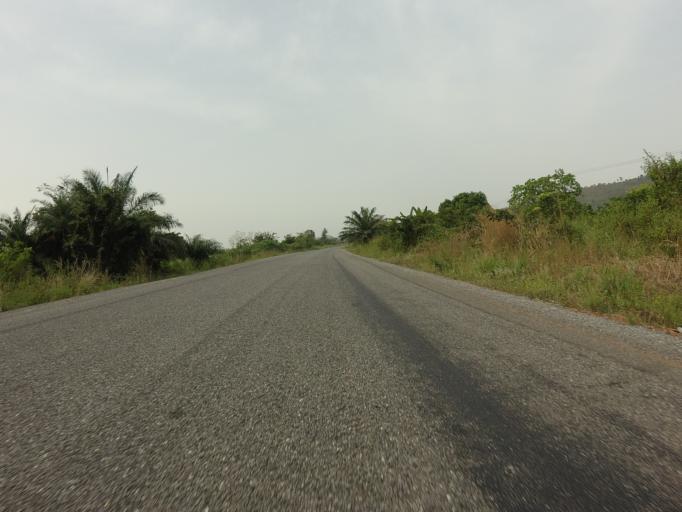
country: GH
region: Volta
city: Ho
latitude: 6.4215
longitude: 0.1865
